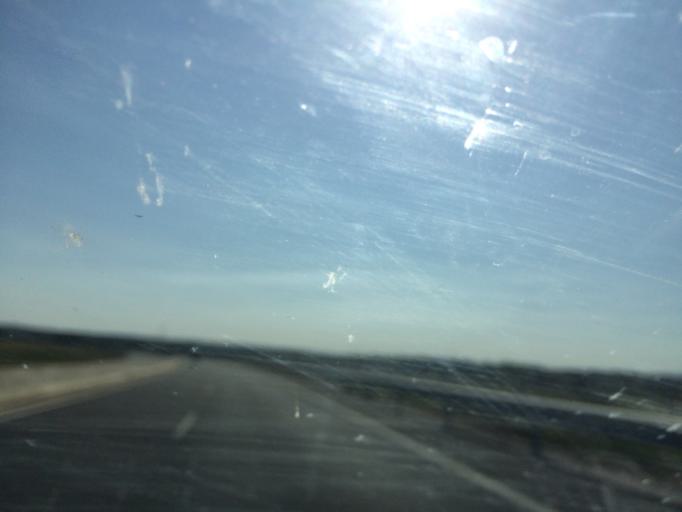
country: ES
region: Madrid
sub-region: Provincia de Madrid
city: Fuente el Saz
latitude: 40.6330
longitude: -3.5401
